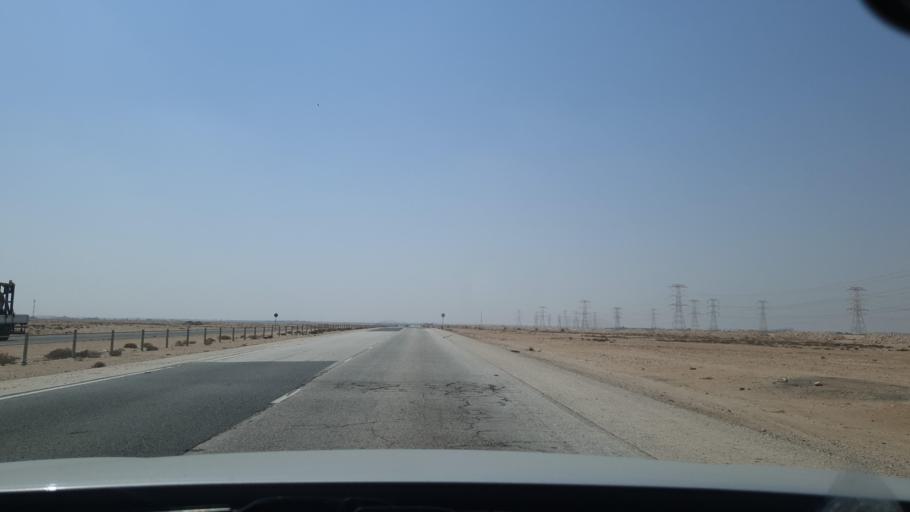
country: QA
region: Al Khawr
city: Al Khawr
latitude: 25.7110
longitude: 51.4477
